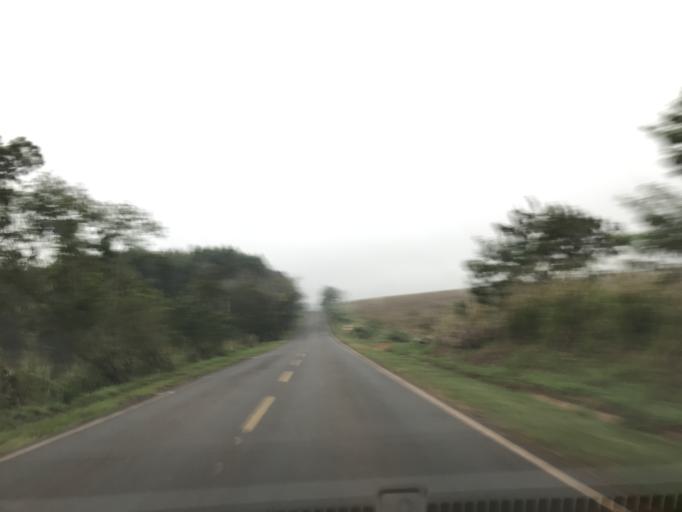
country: PY
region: Canindeyu
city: Salto del Guaira
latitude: -24.0993
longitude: -54.1012
